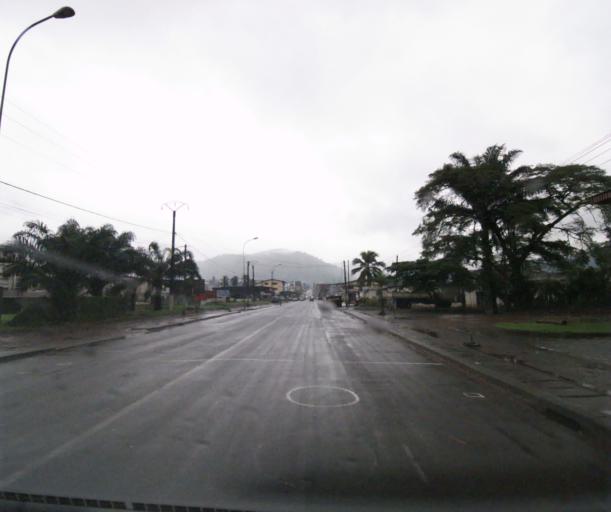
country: CM
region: South-West Province
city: Limbe
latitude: 4.0074
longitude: 9.2123
